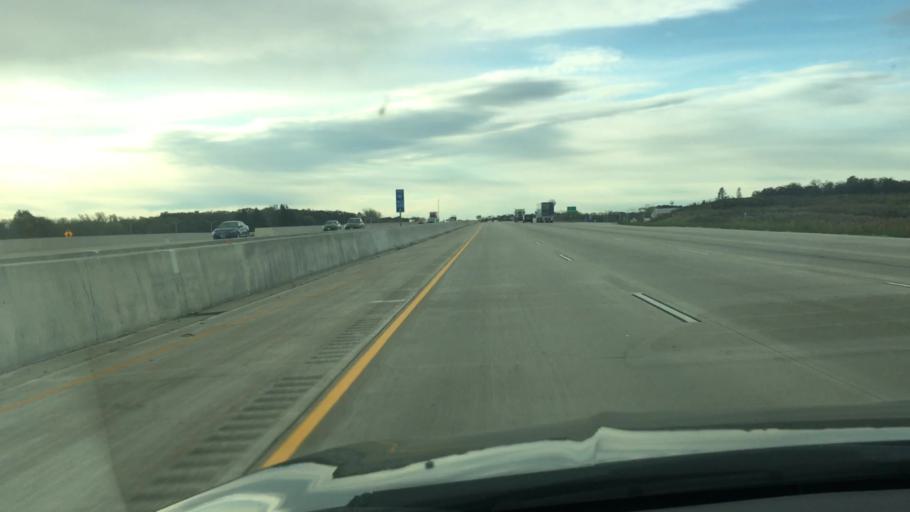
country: US
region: Wisconsin
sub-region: Kenosha County
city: Pleasant Prairie
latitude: 42.5943
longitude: -87.9528
